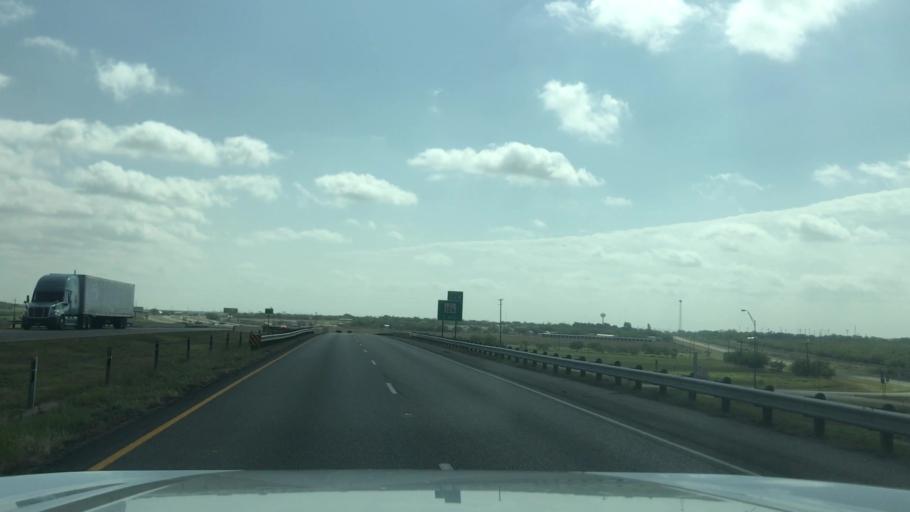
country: US
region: Texas
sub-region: Taylor County
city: Merkel
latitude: 32.4738
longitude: -100.0334
